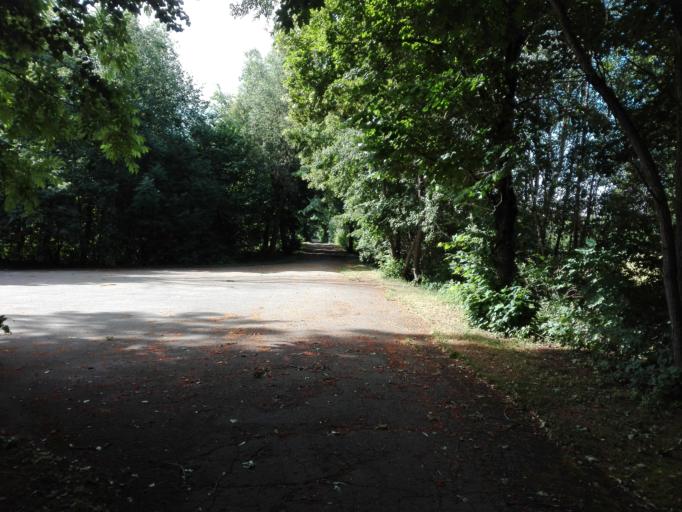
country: LT
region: Panevezys
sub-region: Birzai
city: Birzai
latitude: 56.2238
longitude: 24.7807
